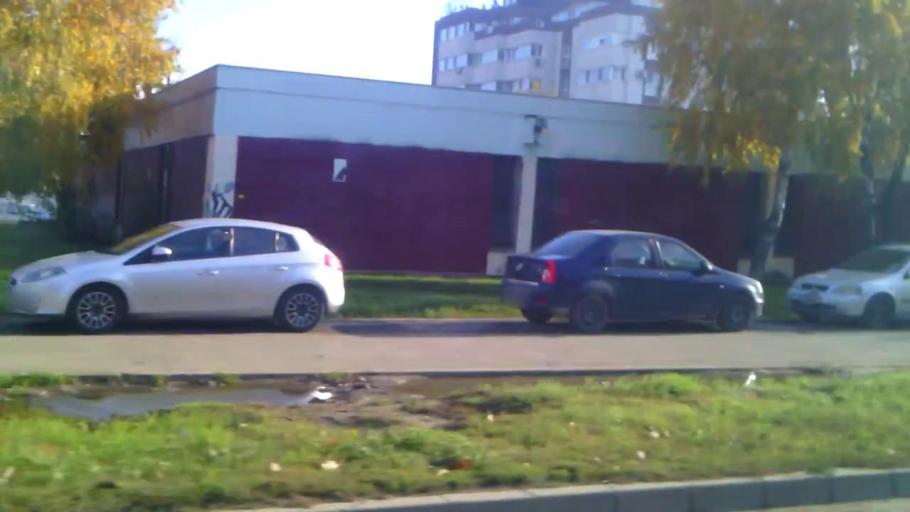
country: RO
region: Ilfov
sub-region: Comuna Popesti-Leordeni
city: Popesti-Leordeni
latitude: 44.3681
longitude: 26.1438
